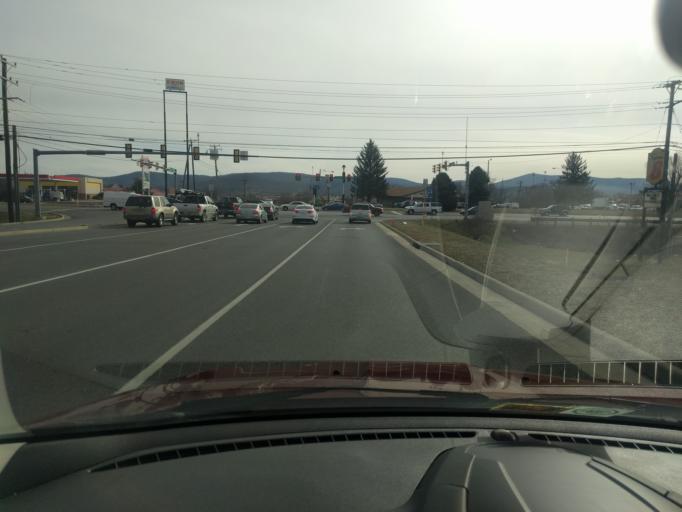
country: US
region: Virginia
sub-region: Augusta County
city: Lyndhurst
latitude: 38.0638
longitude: -78.9373
